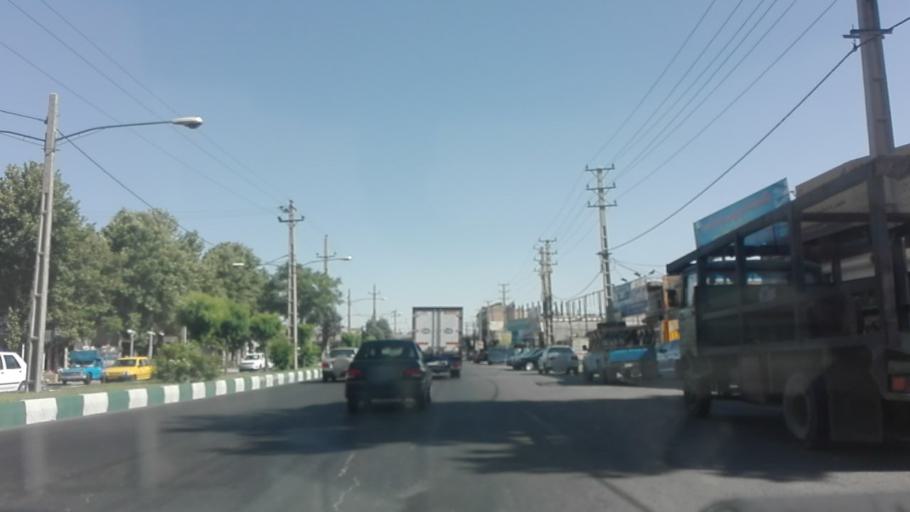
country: IR
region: Tehran
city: Shahriar
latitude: 35.6388
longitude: 51.0643
